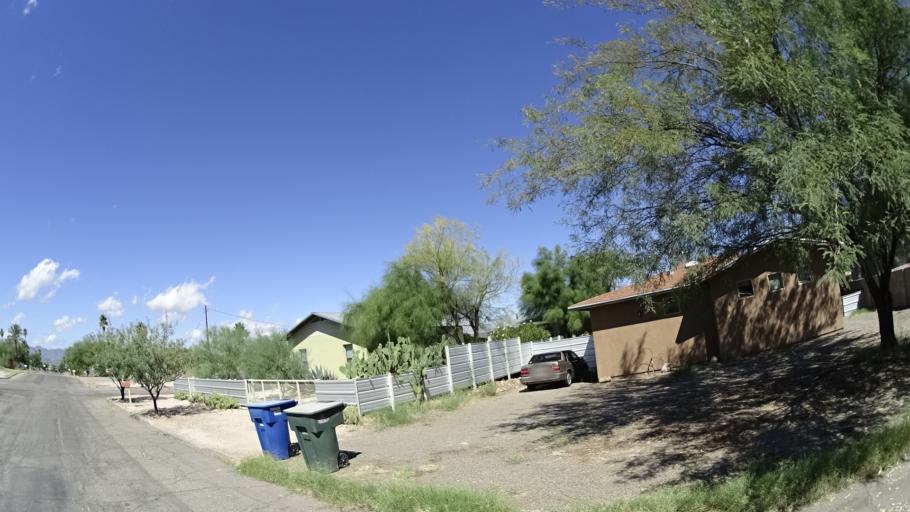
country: US
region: Arizona
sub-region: Pima County
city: Tucson
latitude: 32.2436
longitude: -110.9636
